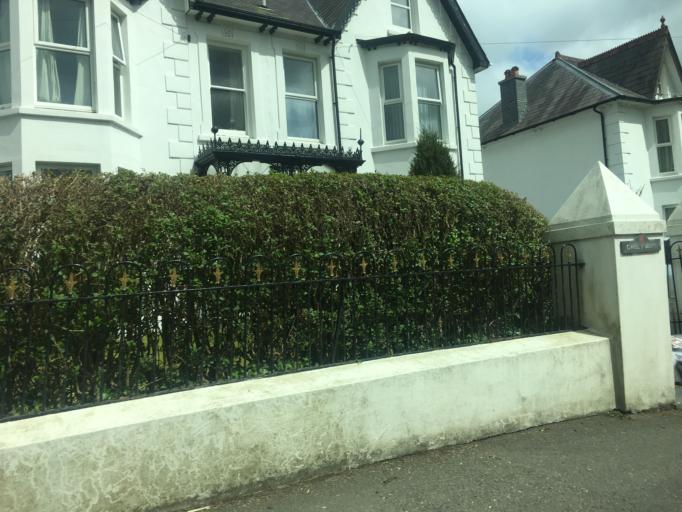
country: GB
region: Wales
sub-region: County of Ceredigion
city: Lampeter
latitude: 52.1164
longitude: -4.0771
